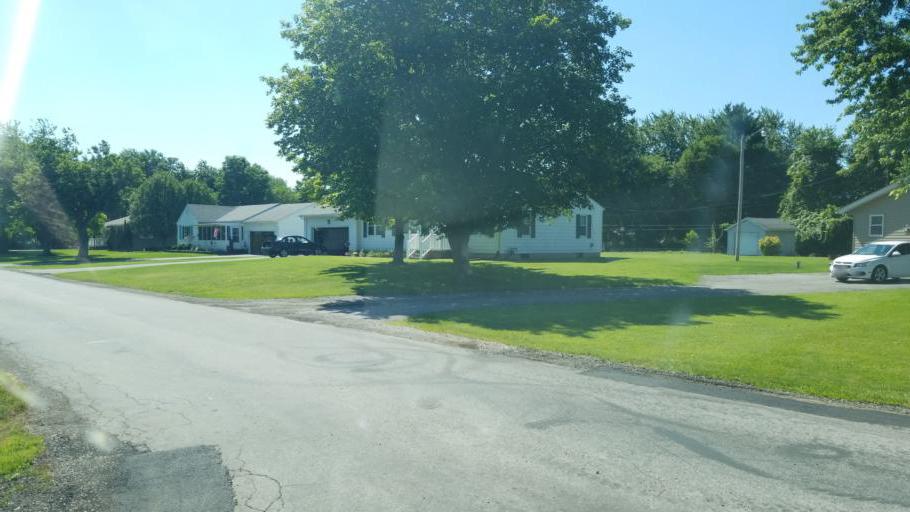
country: US
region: Ohio
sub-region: Marion County
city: Marion
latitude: 40.6520
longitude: -83.1190
